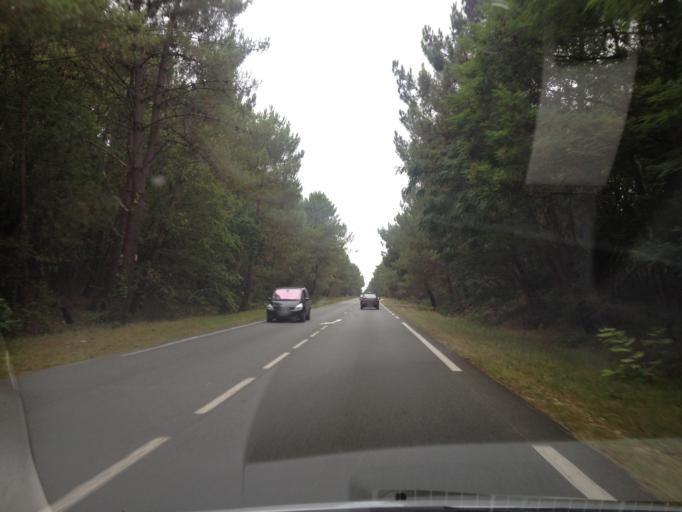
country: FR
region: Poitou-Charentes
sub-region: Departement de la Charente-Maritime
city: Saint-Palais-sur-Mer
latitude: 45.6625
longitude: -1.0780
